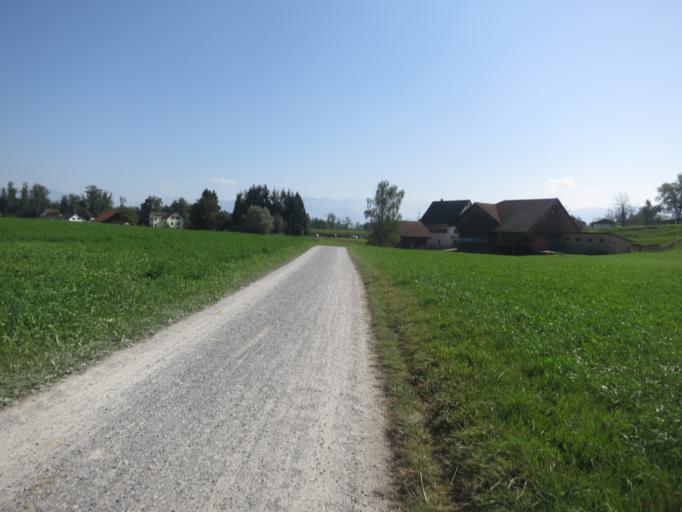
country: CH
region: Zurich
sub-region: Bezirk Hinwil
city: Bubikon
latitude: 47.2616
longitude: 8.8191
